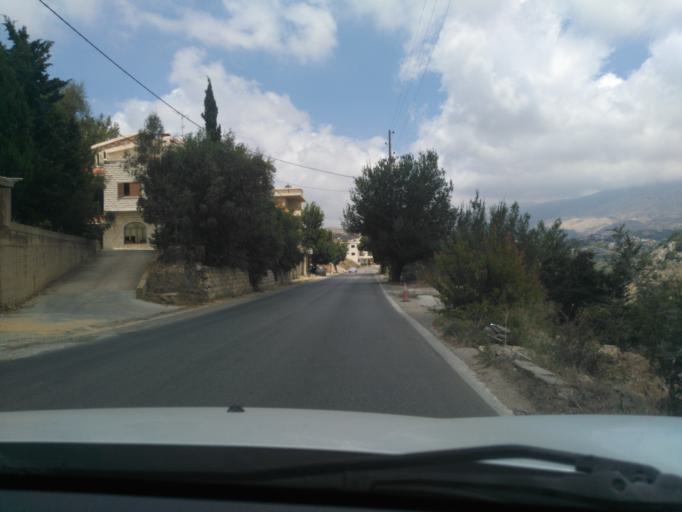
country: LB
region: Mont-Liban
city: Beit ed Dine
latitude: 33.6993
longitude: 35.6582
